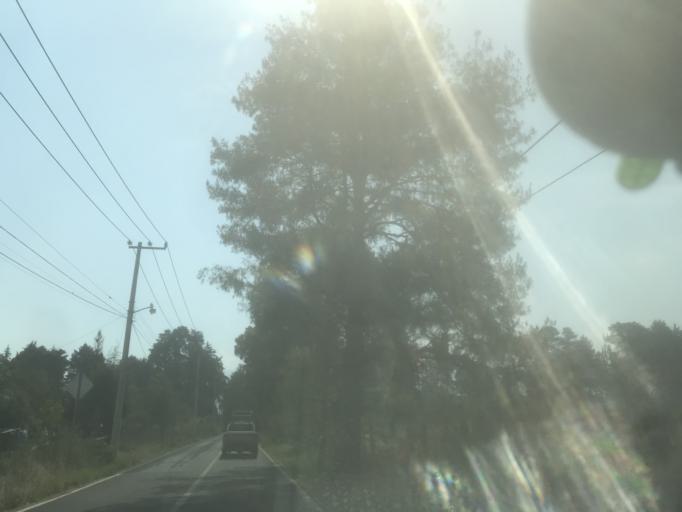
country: MX
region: Mexico
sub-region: Ecatzingo
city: San Marcos Tecomaxusco
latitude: 18.9990
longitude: -98.7710
